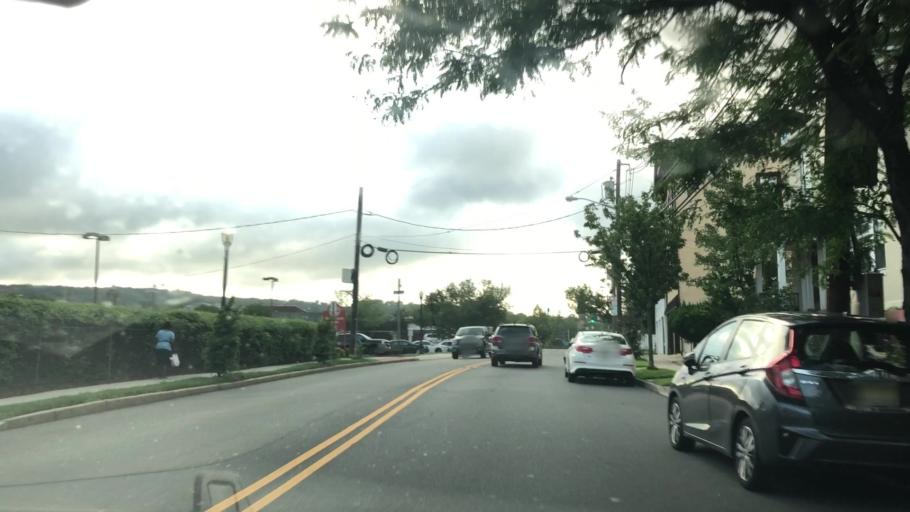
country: US
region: New Jersey
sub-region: Essex County
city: Glen Ridge
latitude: 40.8108
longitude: -74.2107
